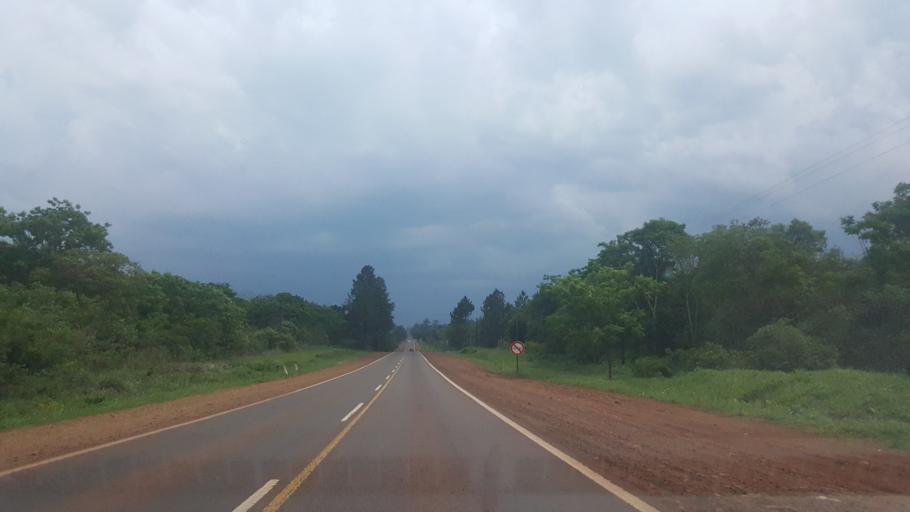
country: AR
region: Misiones
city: Gobernador Roca
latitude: -27.1722
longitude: -55.4485
